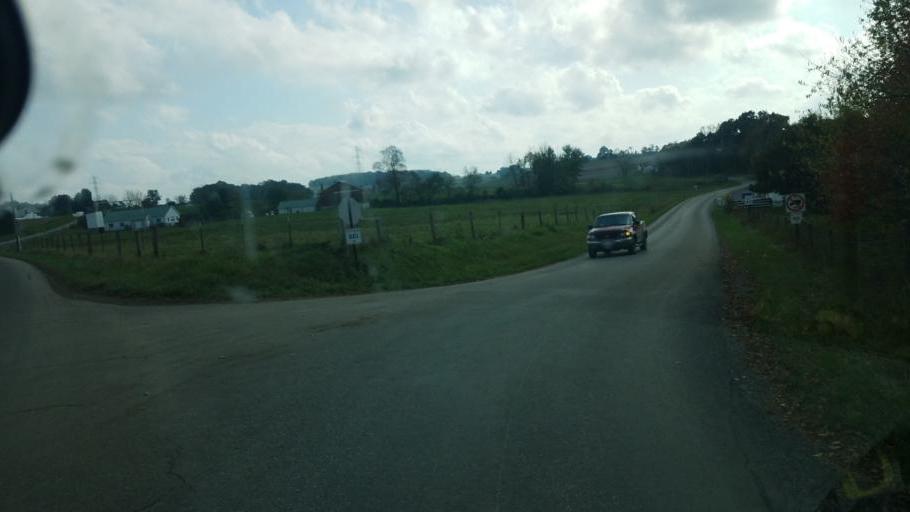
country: US
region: Ohio
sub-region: Wayne County
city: Apple Creek
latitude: 40.6611
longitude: -81.8599
